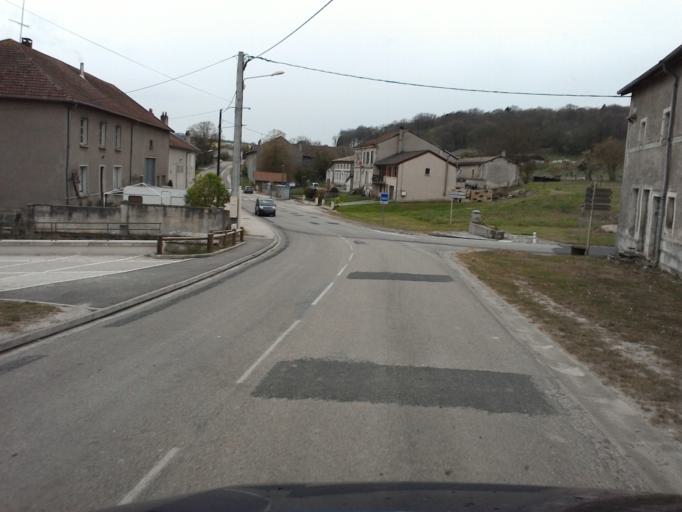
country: FR
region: Lorraine
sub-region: Departement de la Meuse
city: Gondrecourt-le-Chateau
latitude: 48.5689
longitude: 5.5458
